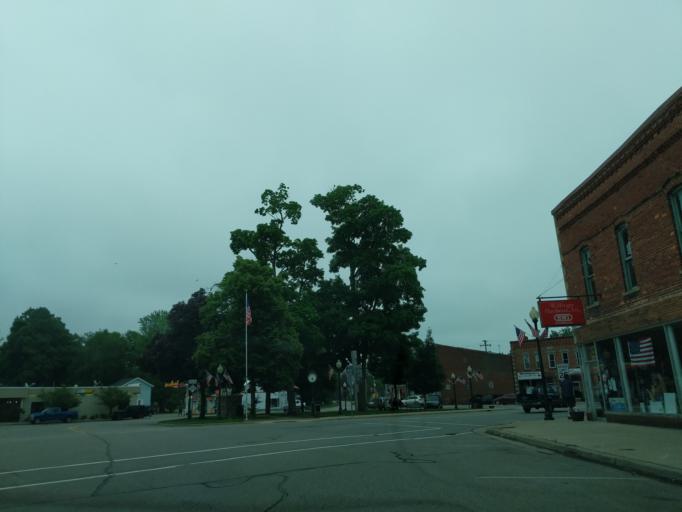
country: US
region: Michigan
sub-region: Hillsdale County
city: Litchfield
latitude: 42.0444
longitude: -84.7587
